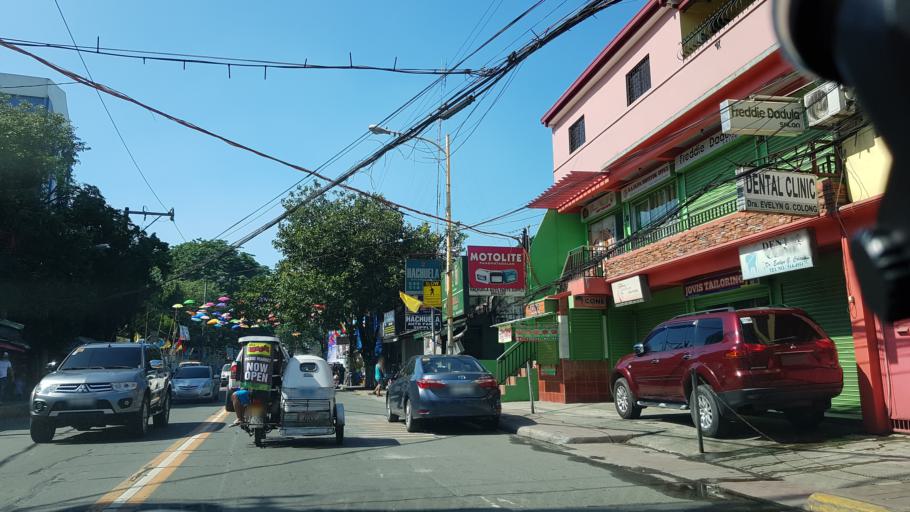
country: PH
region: Calabarzon
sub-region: Province of Rizal
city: Pateros
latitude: 14.5663
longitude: 121.0857
